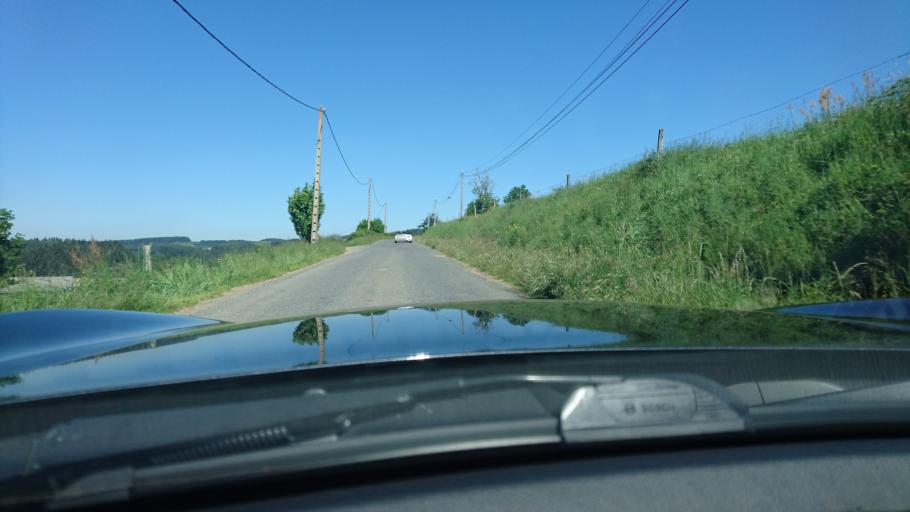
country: FR
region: Rhone-Alpes
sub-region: Departement de la Loire
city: Violay
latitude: 45.8324
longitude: 4.3726
